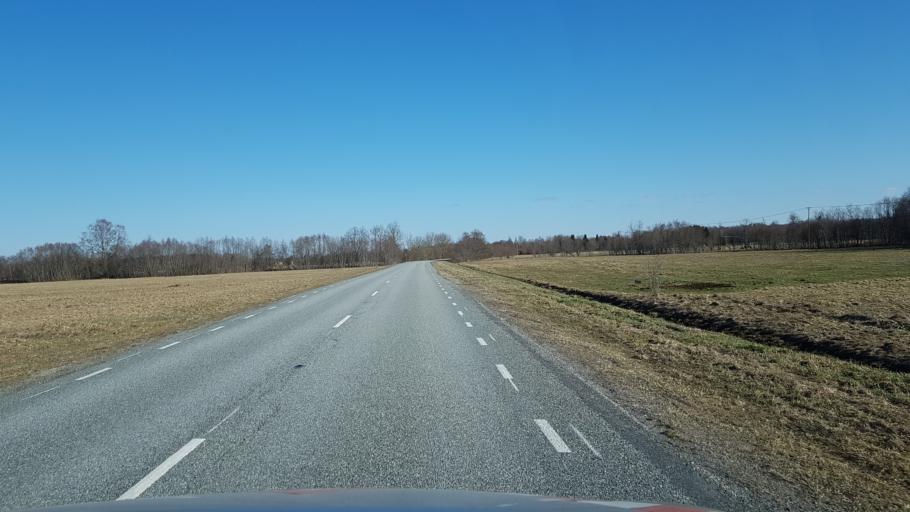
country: EE
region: Laeaene-Virumaa
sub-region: Haljala vald
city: Haljala
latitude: 59.5008
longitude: 26.1300
